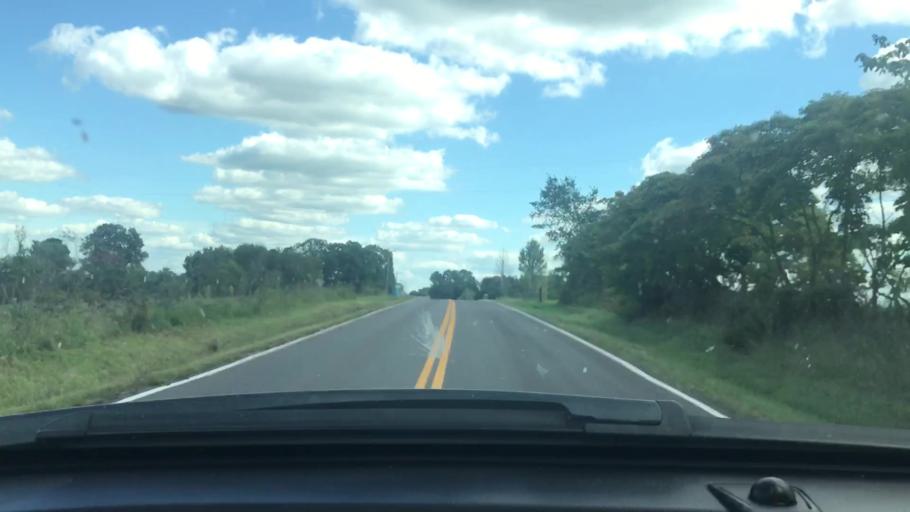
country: US
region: Missouri
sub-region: Wright County
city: Mountain Grove
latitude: 37.3130
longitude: -92.3185
